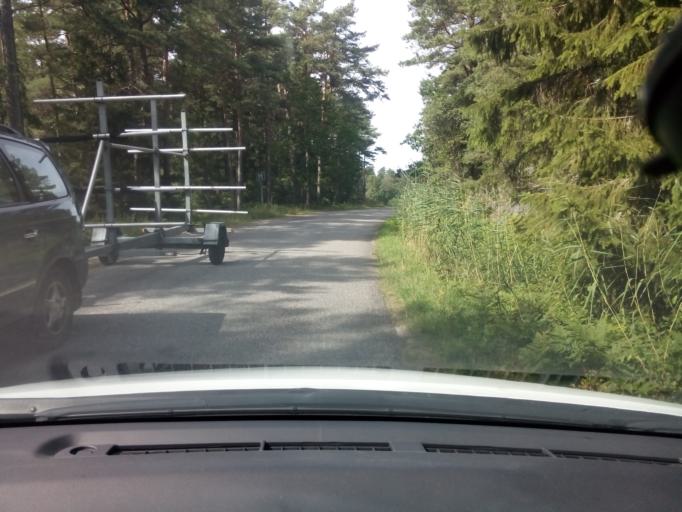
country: SE
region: Soedermanland
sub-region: Trosa Kommun
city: Trosa
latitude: 58.7460
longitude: 17.3840
